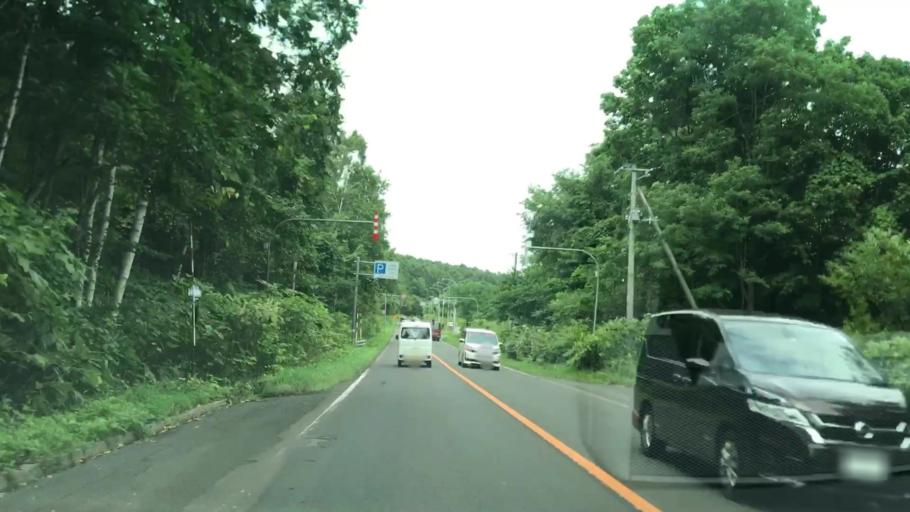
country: JP
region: Hokkaido
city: Niseko Town
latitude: 42.9490
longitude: 140.7016
